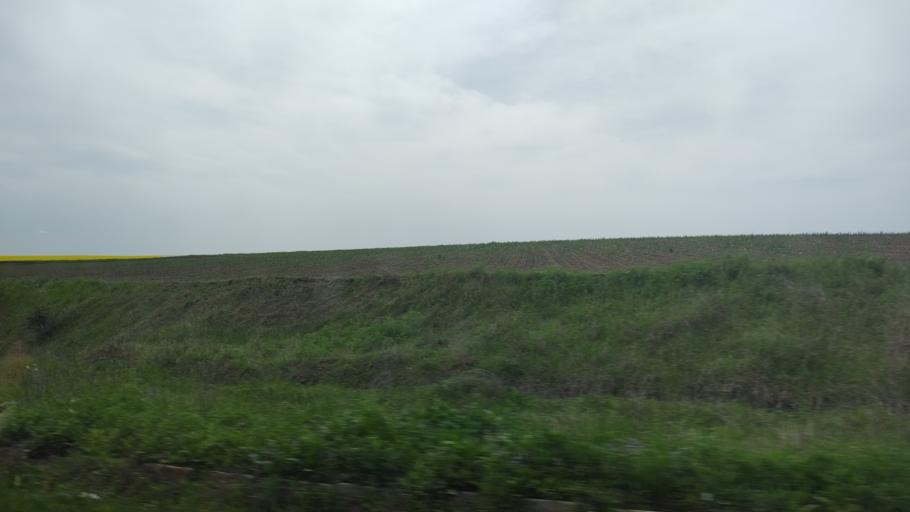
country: RO
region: Constanta
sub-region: Comuna Deleni
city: Pietreni
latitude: 44.0844
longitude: 28.1247
